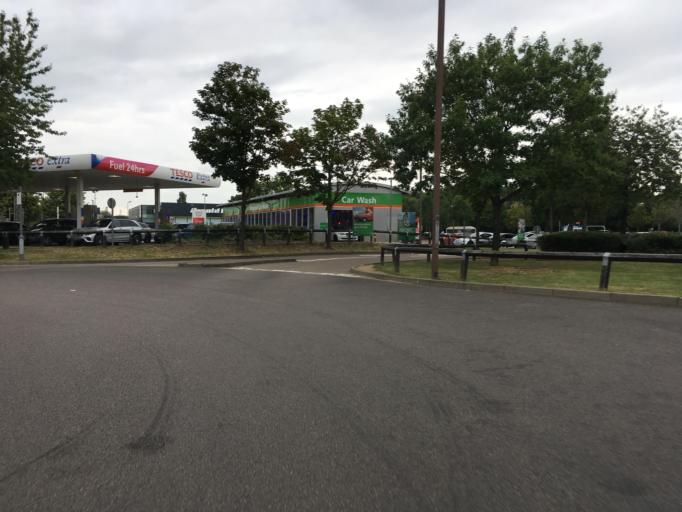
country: GB
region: England
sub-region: Milton Keynes
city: Broughton
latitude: 52.0362
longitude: -0.6899
